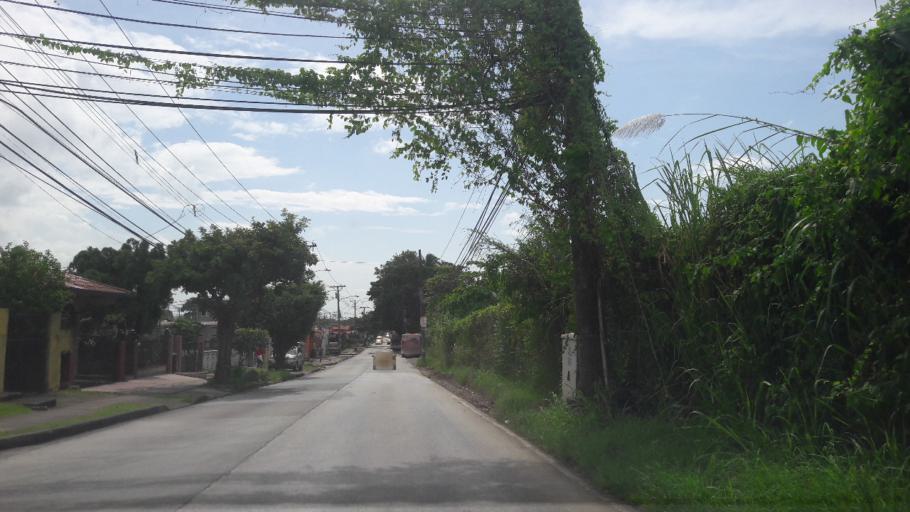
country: PA
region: Panama
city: Tocumen
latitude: 9.0611
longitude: -79.4207
